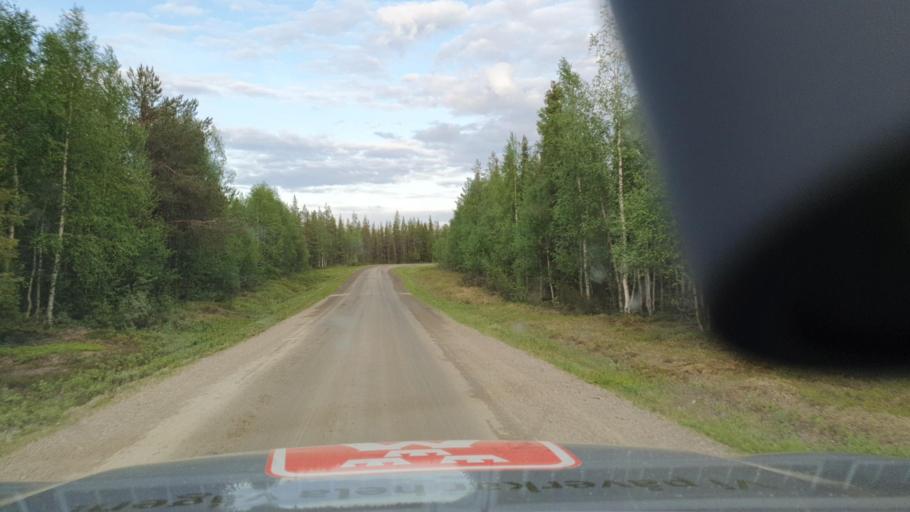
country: SE
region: Norrbotten
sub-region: Gallivare Kommun
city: Gaellivare
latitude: 66.6838
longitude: 21.1891
